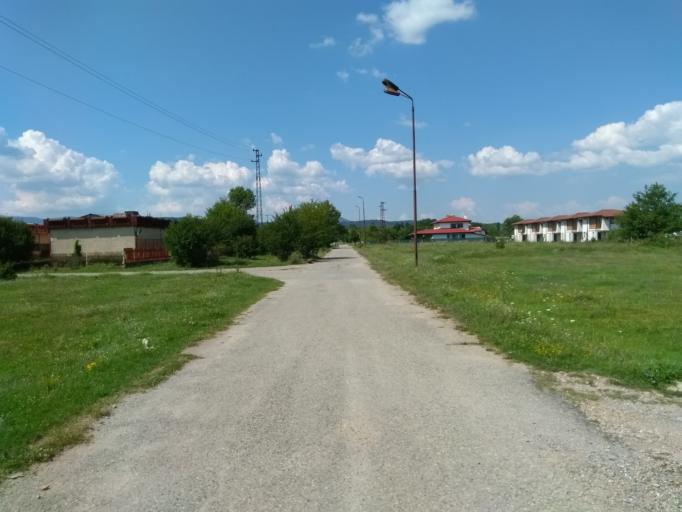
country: BG
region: Stara Zagora
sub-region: Obshtina Pavel Banya
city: Pavel Banya
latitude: 42.6017
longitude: 25.2189
